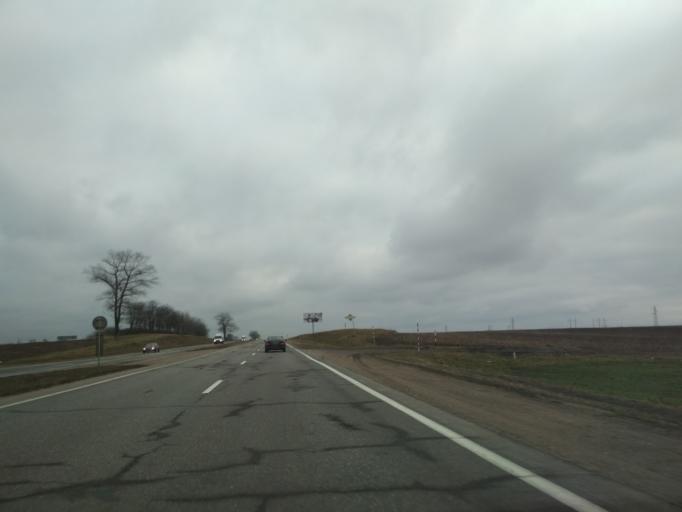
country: BY
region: Minsk
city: Dukora
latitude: 53.6880
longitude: 27.9088
